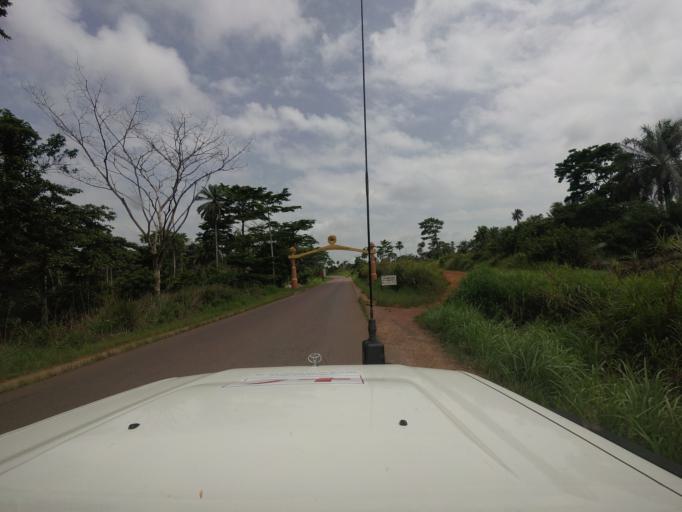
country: GN
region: Nzerekore
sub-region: Nzerekore Prefecture
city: Nzerekore
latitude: 7.7398
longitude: -8.7538
